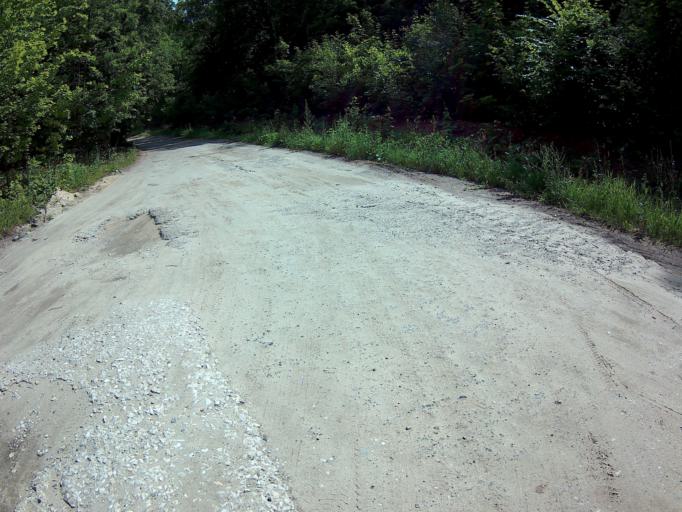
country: RU
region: Nizjnij Novgorod
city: Nizhniy Novgorod
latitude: 56.2251
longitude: 43.9222
